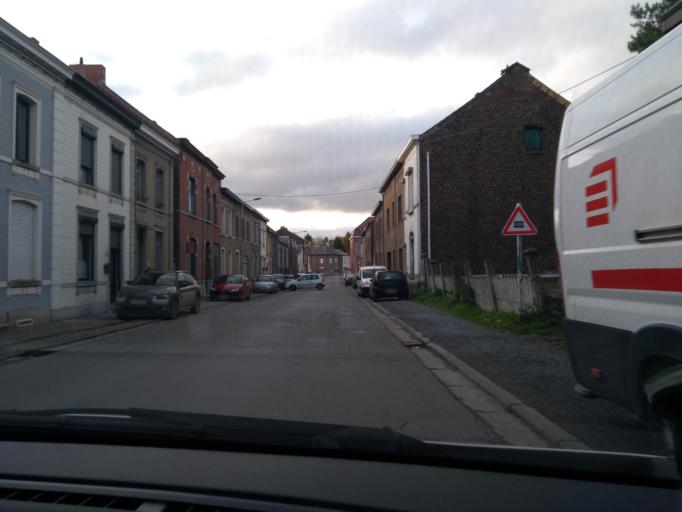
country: BE
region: Wallonia
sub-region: Province du Hainaut
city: Morlanwelz-Mariemont
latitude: 50.4294
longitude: 4.2129
